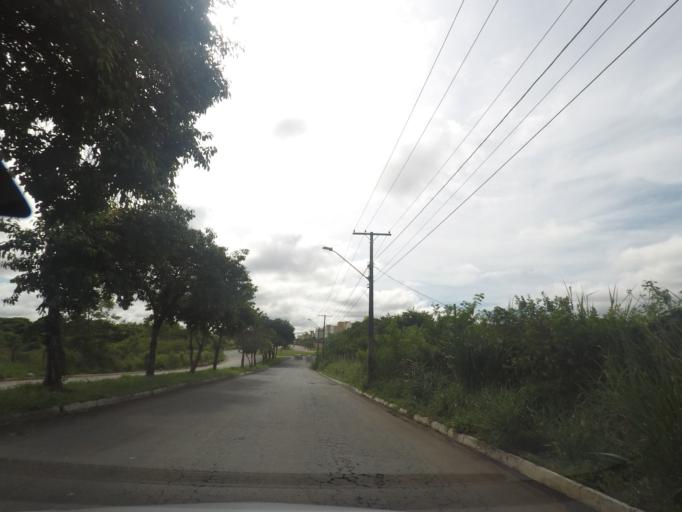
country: BR
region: Goias
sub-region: Goiania
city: Goiania
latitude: -16.6590
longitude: -49.2165
